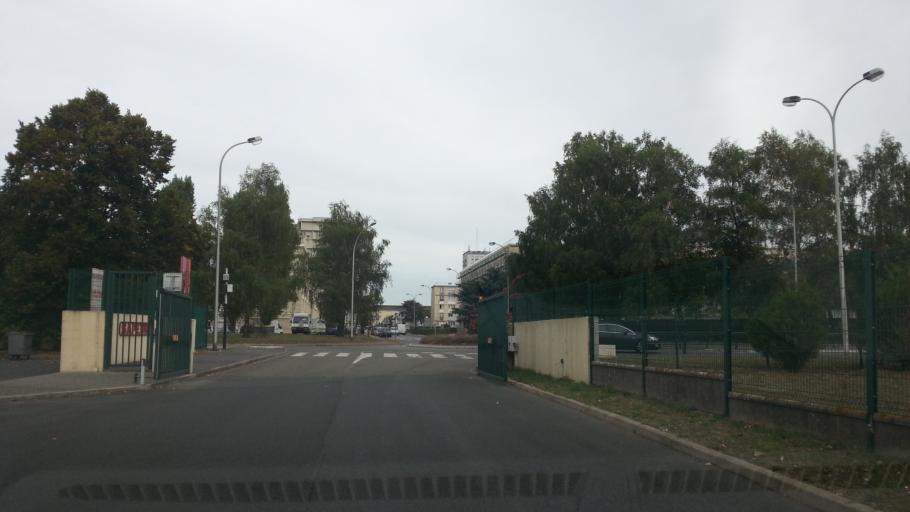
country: FR
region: Picardie
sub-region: Departement de l'Oise
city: Creil
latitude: 49.2485
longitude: 2.4674
